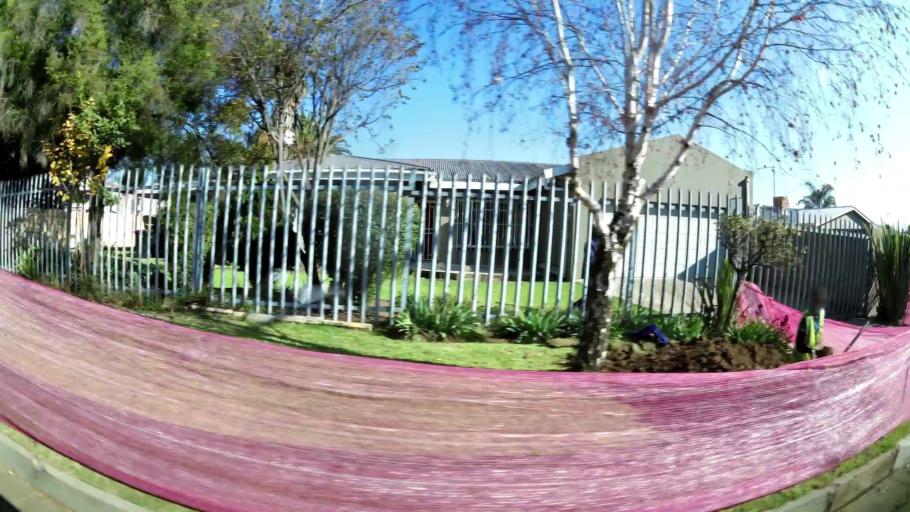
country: ZA
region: Gauteng
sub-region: Ekurhuleni Metropolitan Municipality
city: Benoni
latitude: -26.1522
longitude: 28.3108
